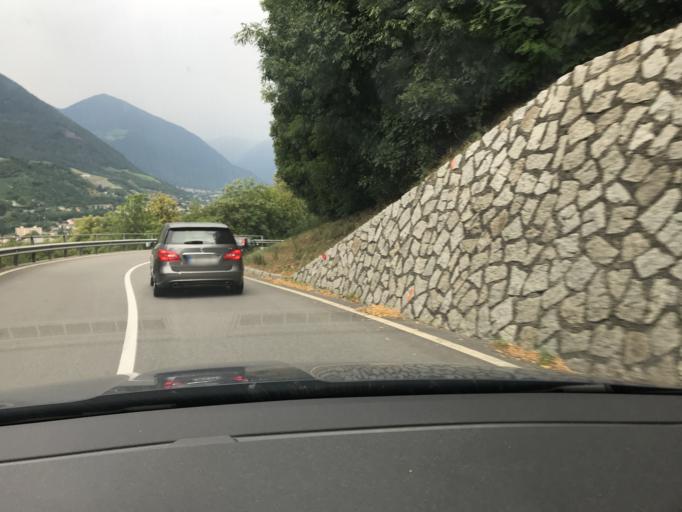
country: IT
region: Trentino-Alto Adige
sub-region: Bolzano
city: Bressanone
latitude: 46.6976
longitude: 11.6594
